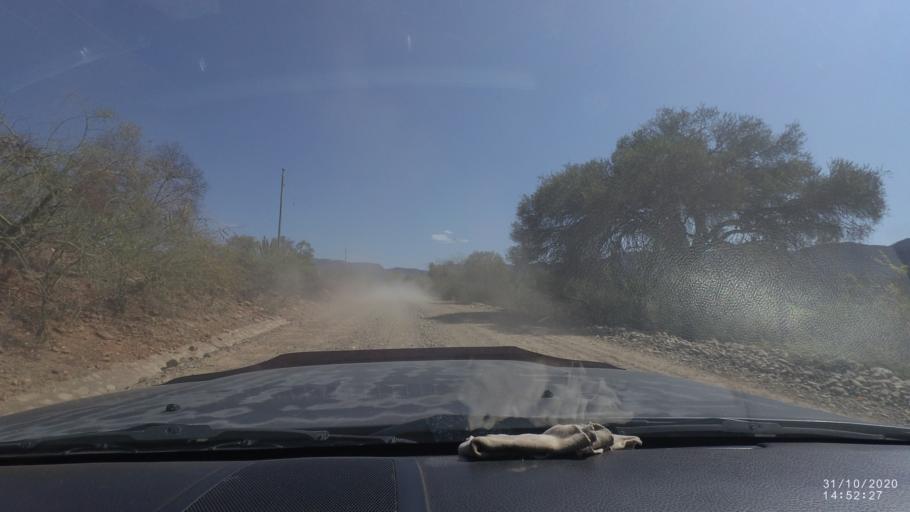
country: BO
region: Cochabamba
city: Aiquile
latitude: -18.2139
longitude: -64.8567
